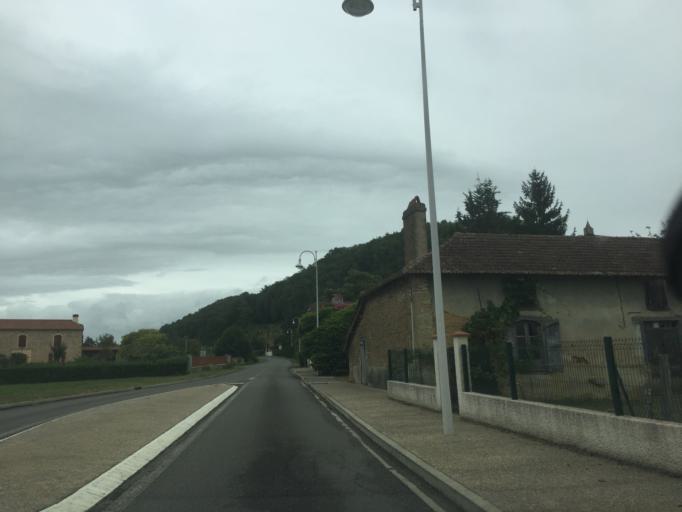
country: FR
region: Midi-Pyrenees
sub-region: Departement des Hautes-Pyrenees
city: Rabastens-de-Bigorre
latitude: 43.3775
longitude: 0.2114
